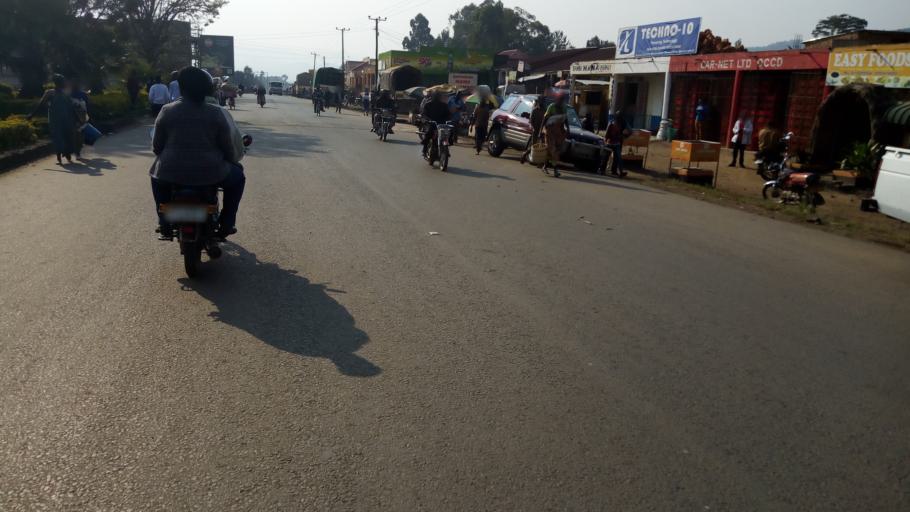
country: UG
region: Western Region
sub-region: Kisoro District
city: Kisoro
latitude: -1.2825
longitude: 29.6961
